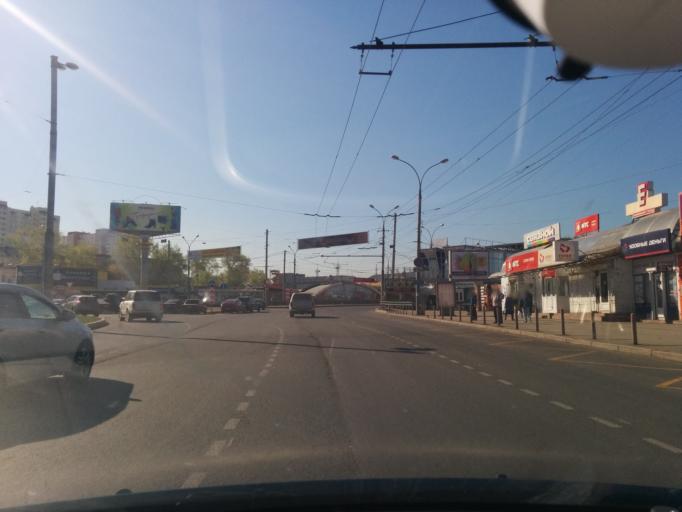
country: RU
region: Perm
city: Perm
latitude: 58.0033
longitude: 56.2307
